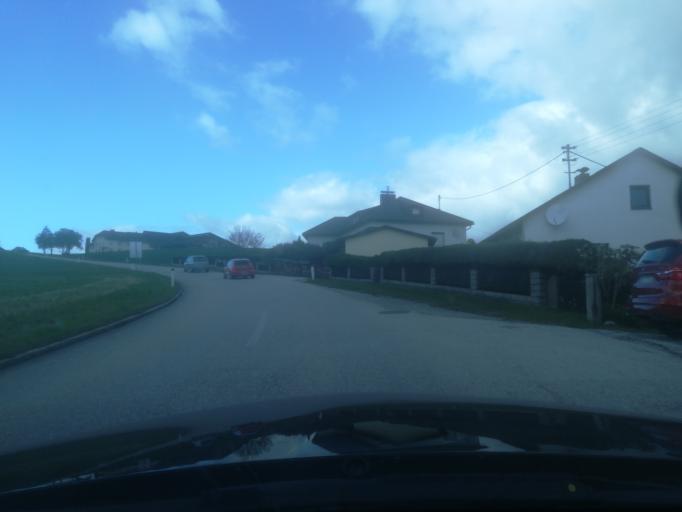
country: AT
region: Upper Austria
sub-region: Linz Stadt
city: Linz
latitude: 48.3522
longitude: 14.2631
